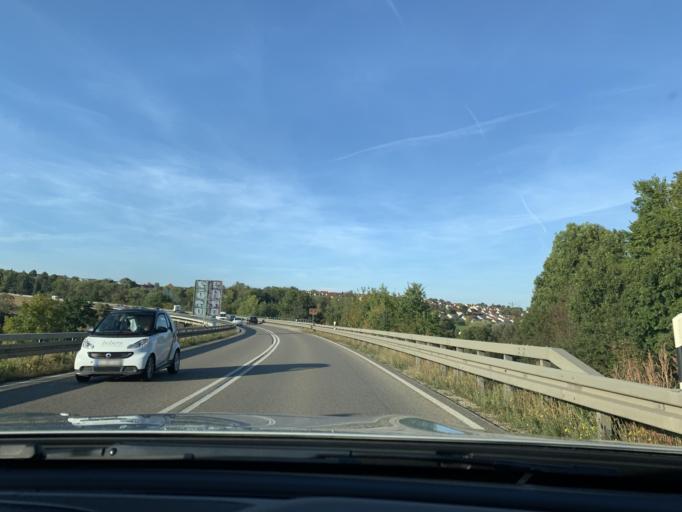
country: DE
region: Baden-Wuerttemberg
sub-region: Regierungsbezirk Stuttgart
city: Neckartailfingen
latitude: 48.6225
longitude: 9.2494
